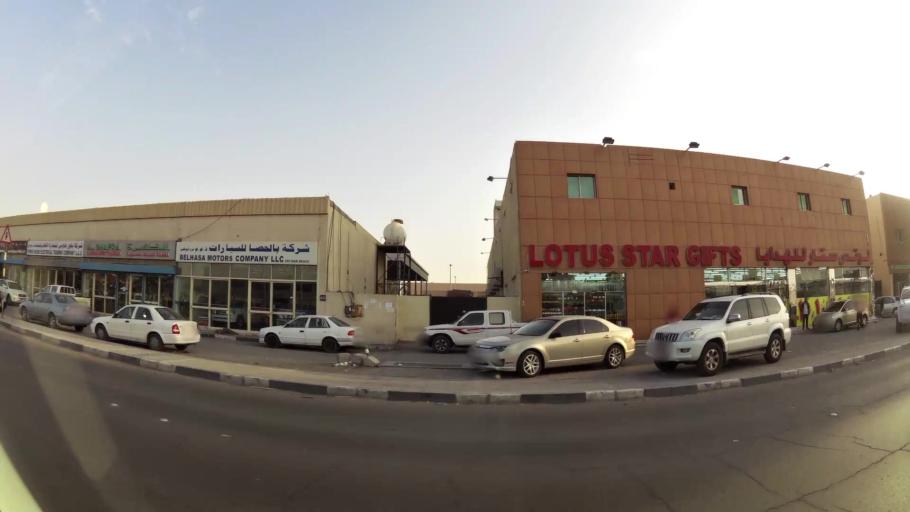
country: AE
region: Abu Dhabi
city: Abu Dhabi
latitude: 24.3728
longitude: 54.5059
